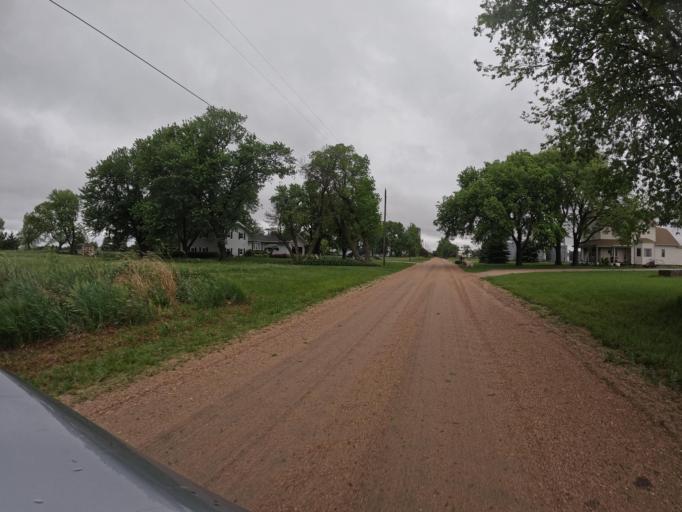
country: US
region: Nebraska
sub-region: Clay County
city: Harvard
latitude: 40.6275
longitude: -98.0968
